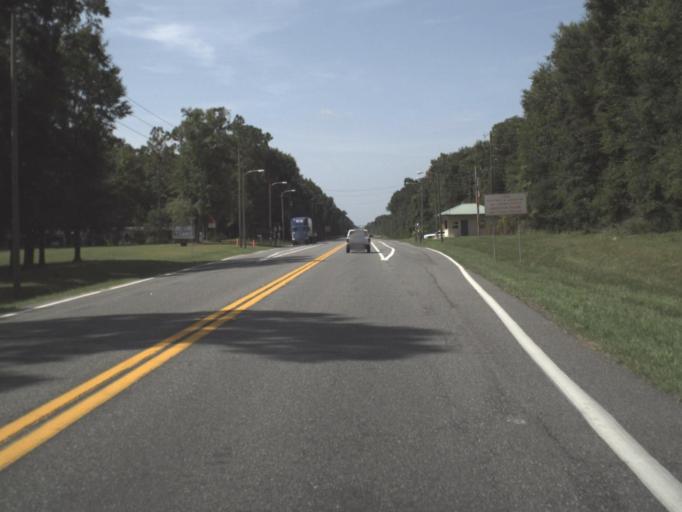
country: US
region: Florida
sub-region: Lafayette County
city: Mayo
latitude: 30.1208
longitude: -83.1698
